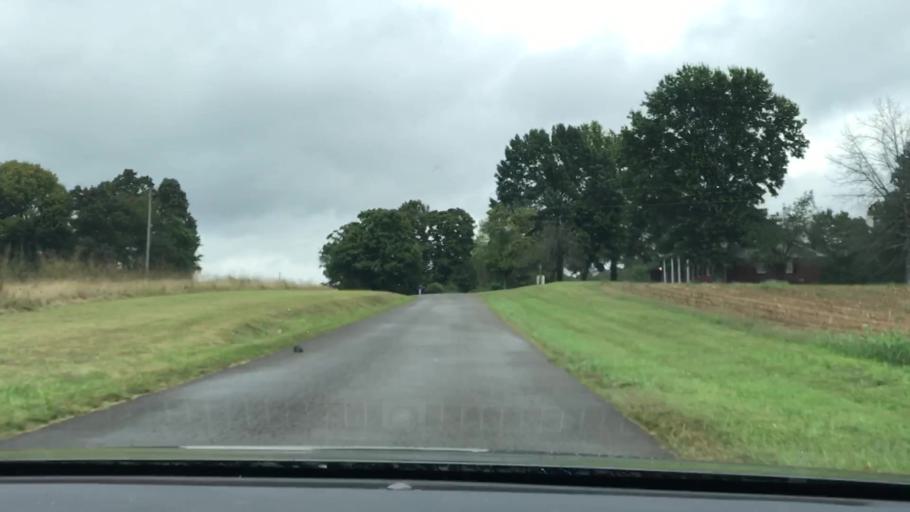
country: US
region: Kentucky
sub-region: Monroe County
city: Tompkinsville
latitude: 36.6263
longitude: -85.7711
